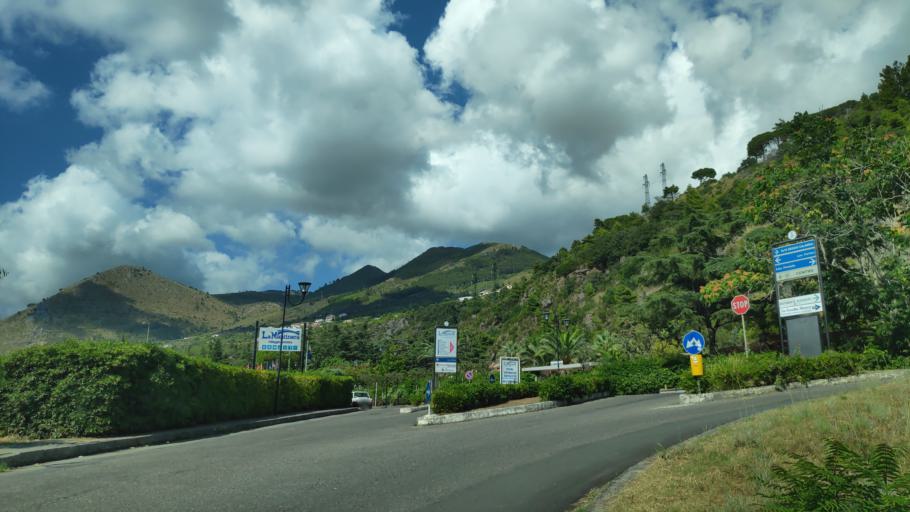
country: IT
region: Calabria
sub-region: Provincia di Cosenza
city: Praia a Mare
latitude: 39.8754
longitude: 15.7877
